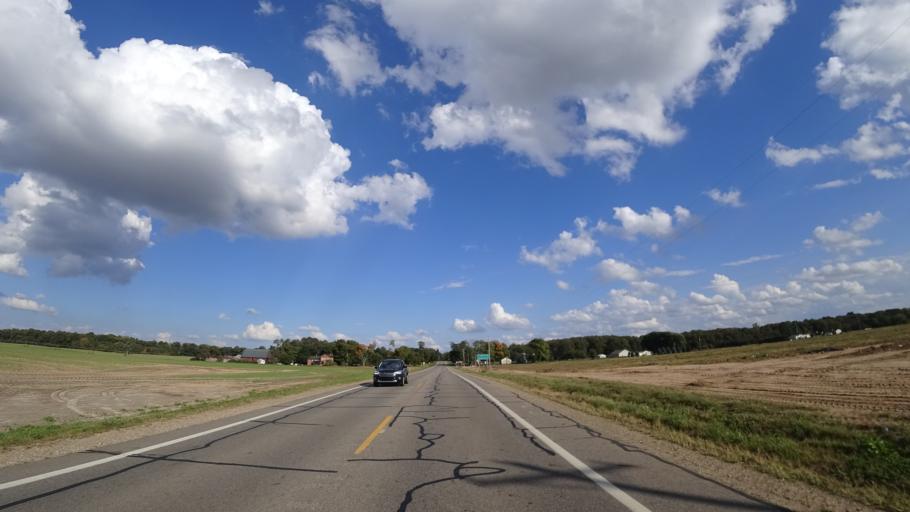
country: US
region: Michigan
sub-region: Saint Joseph County
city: Centreville
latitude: 41.9258
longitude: -85.5696
